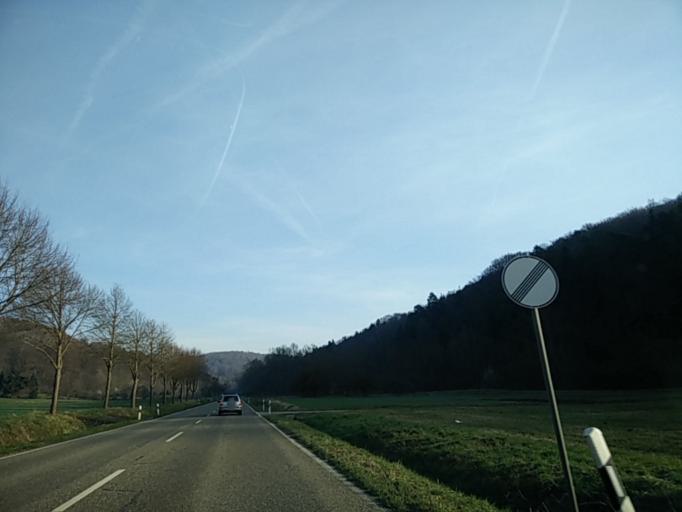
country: DE
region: Baden-Wuerttemberg
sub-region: Tuebingen Region
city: Tuebingen
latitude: 48.5380
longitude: 9.0768
